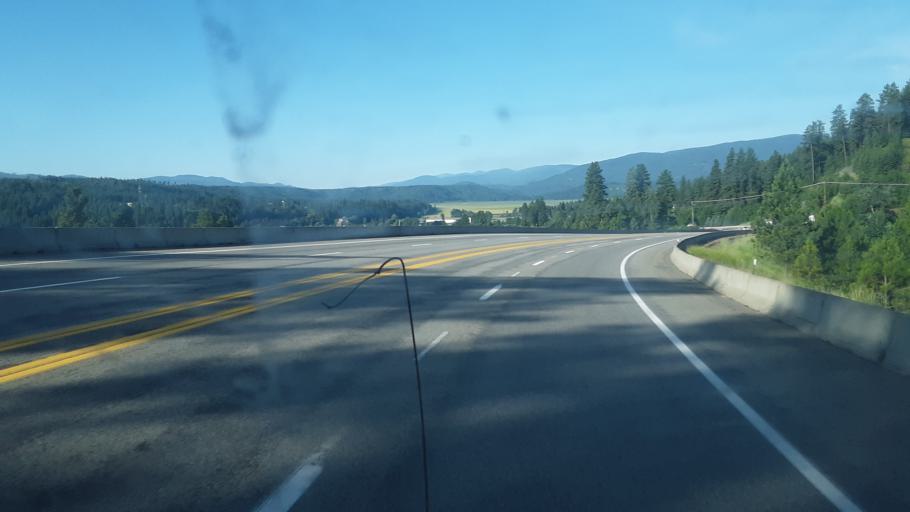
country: US
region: Idaho
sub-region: Boundary County
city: Bonners Ferry
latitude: 48.7104
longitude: -116.3048
